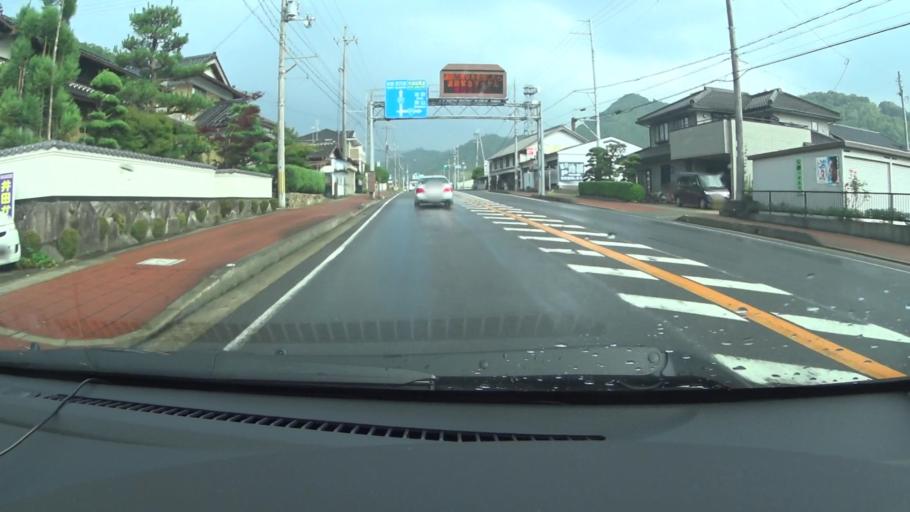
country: JP
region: Kyoto
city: Ayabe
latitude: 35.2944
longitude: 135.2673
